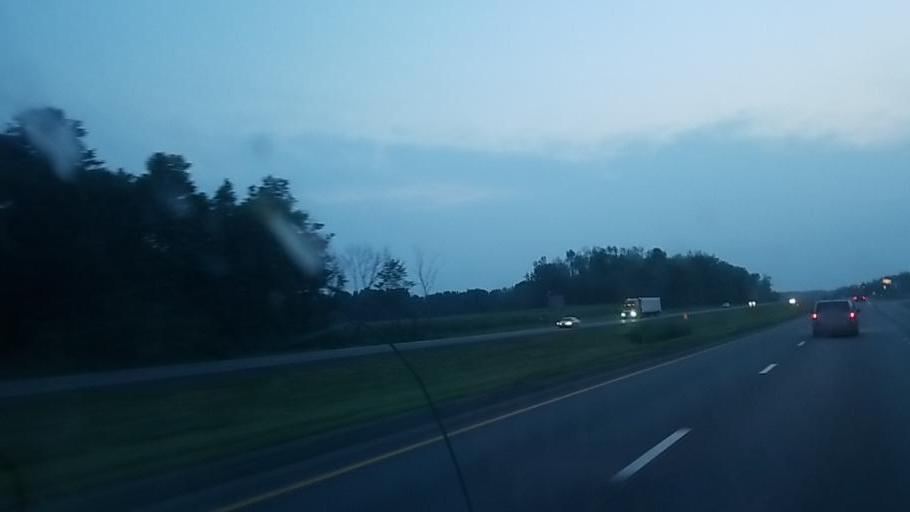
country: US
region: New York
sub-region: Madison County
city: Bolivar
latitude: 43.0950
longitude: -75.8371
